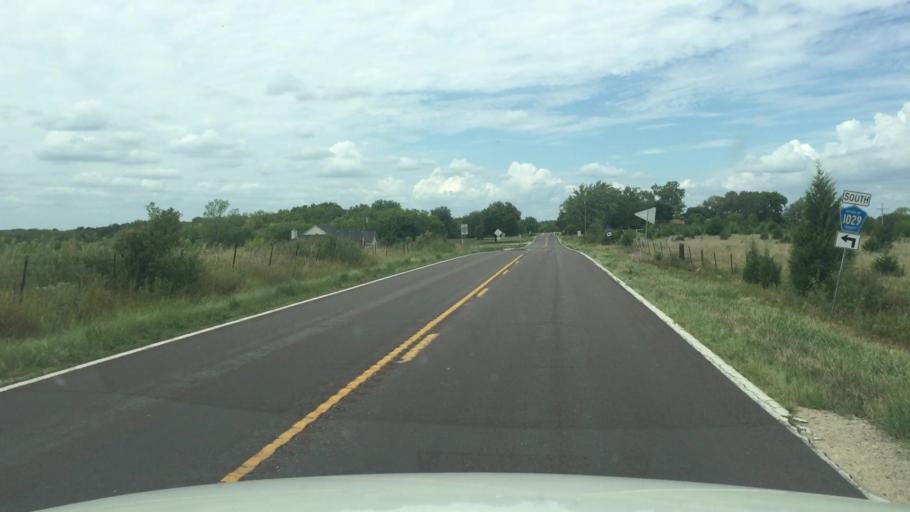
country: US
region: Kansas
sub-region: Douglas County
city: Lawrence
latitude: 38.9943
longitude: -95.3986
